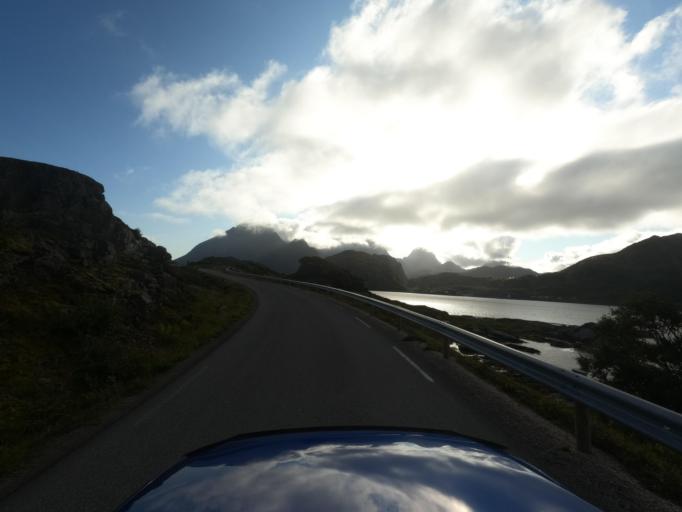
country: NO
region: Nordland
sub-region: Flakstad
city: Ramberg
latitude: 68.0147
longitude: 13.1963
